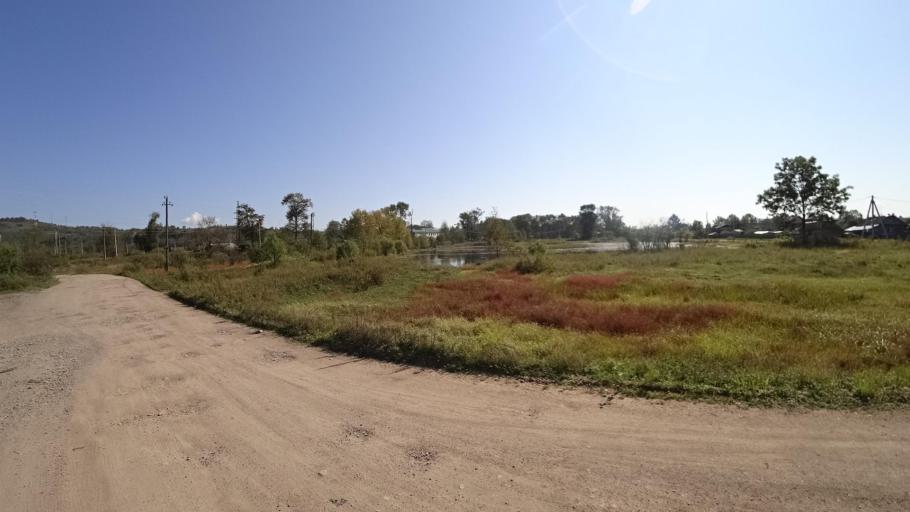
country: RU
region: Jewish Autonomous Oblast
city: Bira
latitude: 49.0005
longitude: 132.4504
